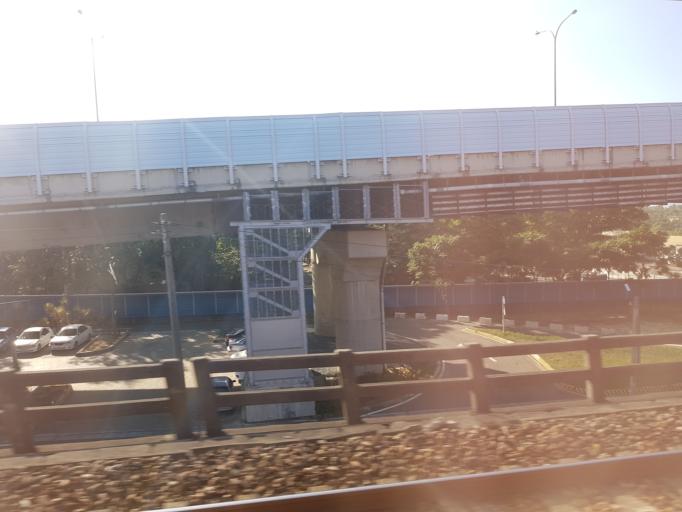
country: TW
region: Taiwan
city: Fengyuan
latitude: 24.3002
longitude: 120.7324
